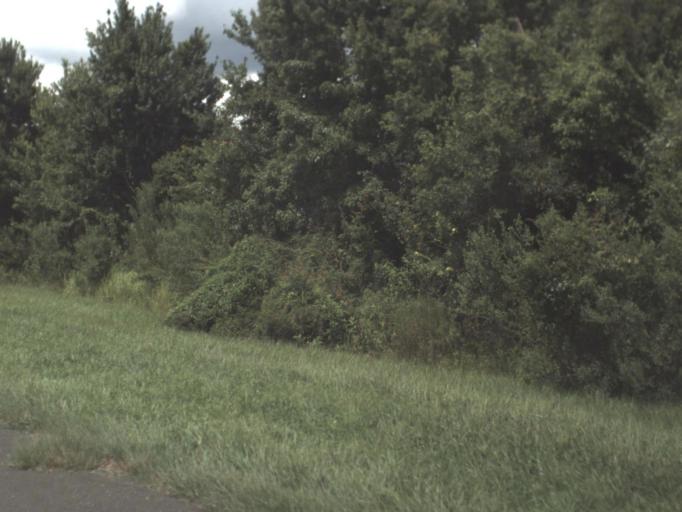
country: US
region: Florida
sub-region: Pasco County
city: Crystal Springs
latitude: 28.1439
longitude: -82.1507
